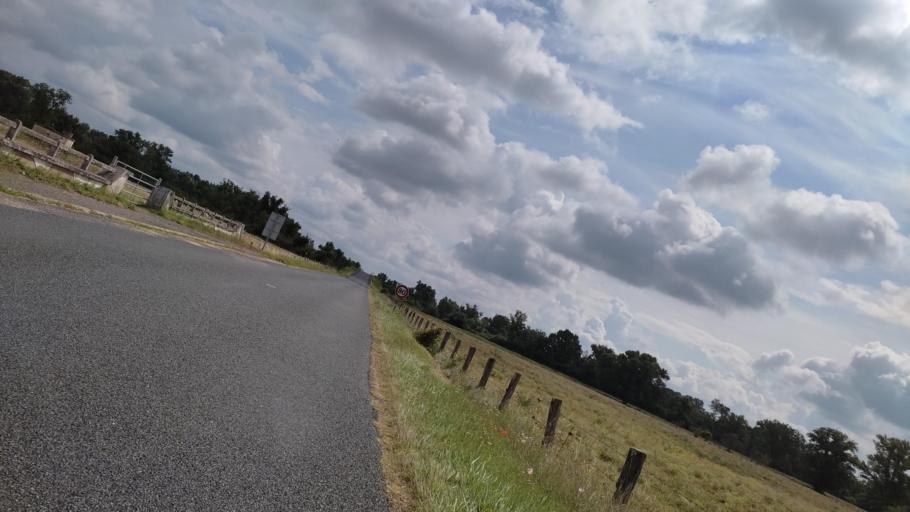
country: FR
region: Auvergne
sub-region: Departement de l'Allier
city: Beaulon
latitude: 46.7288
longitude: 3.6311
